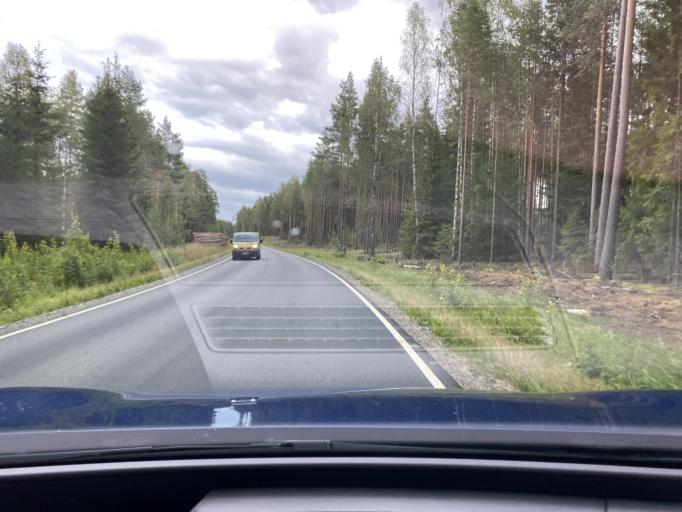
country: FI
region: Pirkanmaa
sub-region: Lounais-Pirkanmaa
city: Vammala
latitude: 61.3001
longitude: 22.9679
